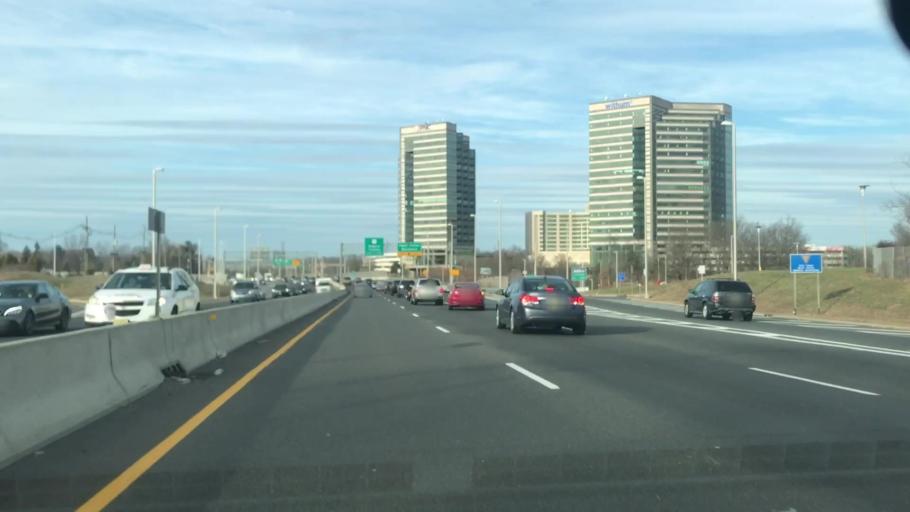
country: US
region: New Jersey
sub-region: Middlesex County
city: Highland Park
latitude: 40.4754
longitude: -74.4097
